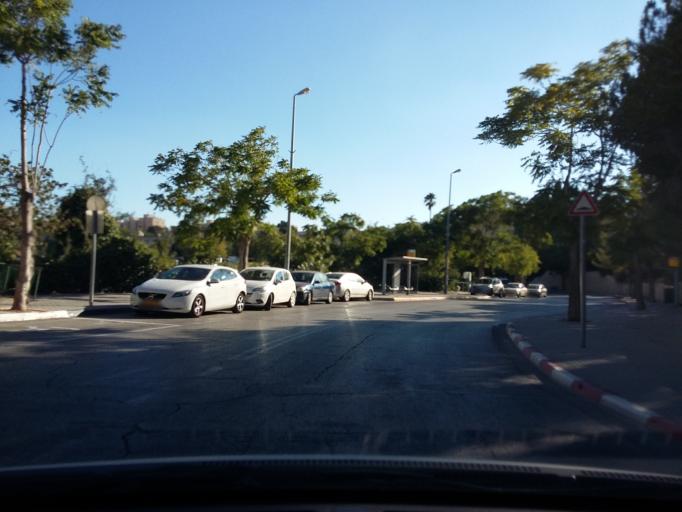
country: PS
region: West Bank
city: `Anata
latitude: 31.8052
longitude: 35.2404
